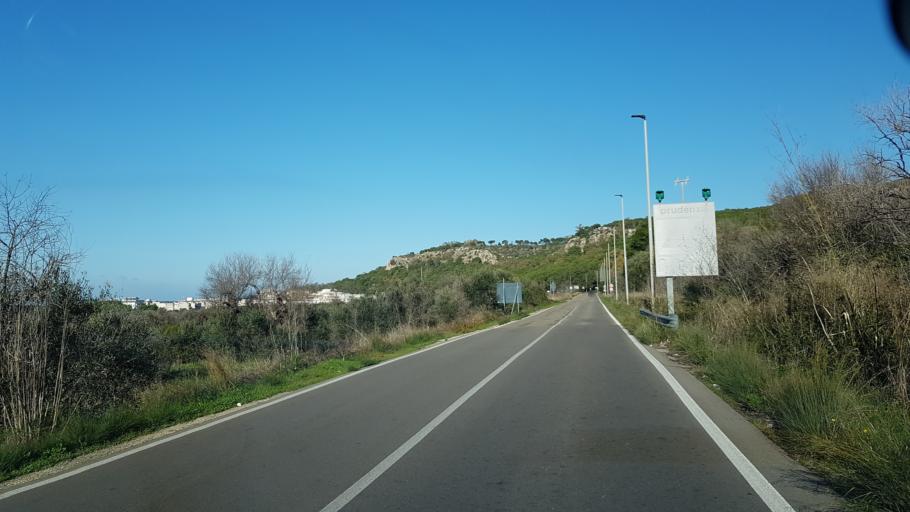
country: IT
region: Apulia
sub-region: Provincia di Lecce
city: Sannicola
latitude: 40.1036
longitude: 18.0193
